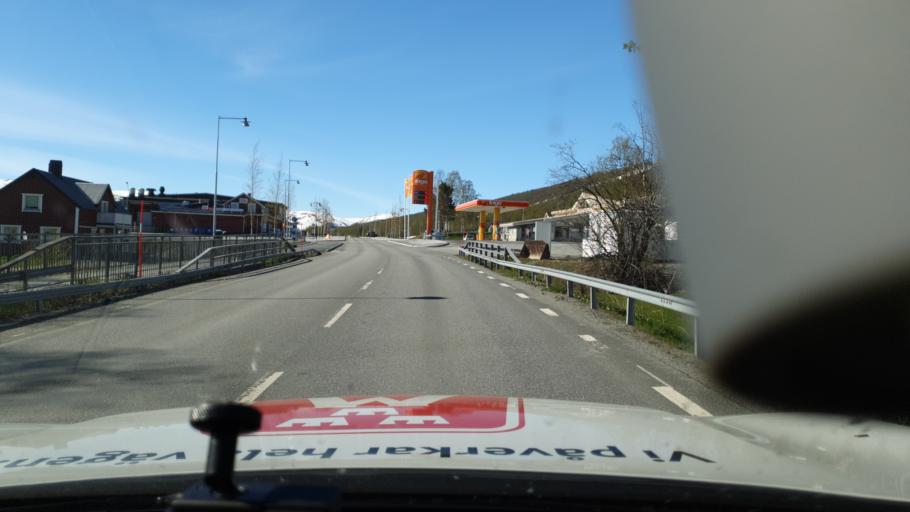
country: NO
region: Nordland
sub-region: Rana
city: Mo i Rana
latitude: 65.8177
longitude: 15.0868
